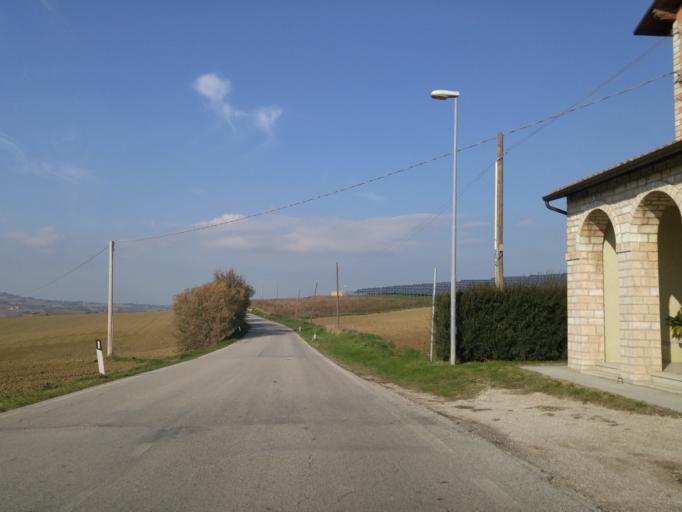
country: IT
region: The Marches
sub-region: Provincia di Pesaro e Urbino
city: Lucrezia
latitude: 43.8019
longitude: 12.9129
